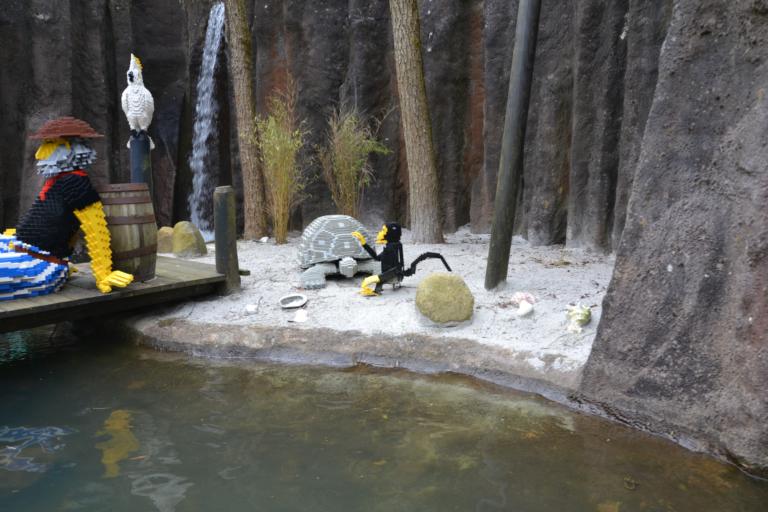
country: DK
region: South Denmark
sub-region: Billund Kommune
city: Billund
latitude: 55.7357
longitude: 9.1257
